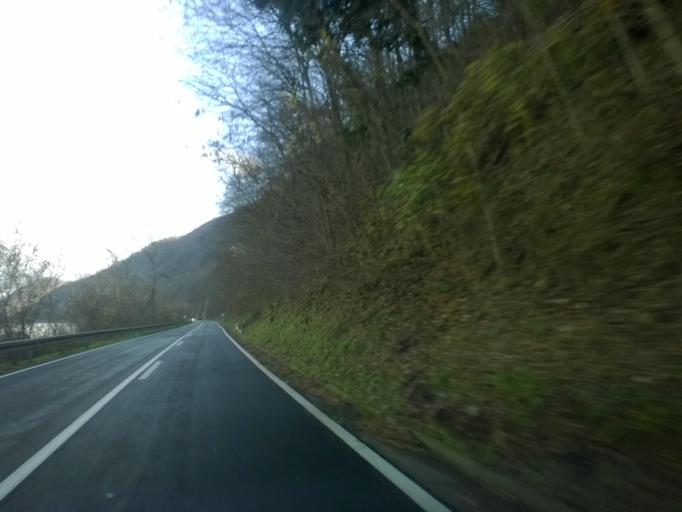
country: RS
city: Radenka
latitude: 44.6451
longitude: 21.8155
